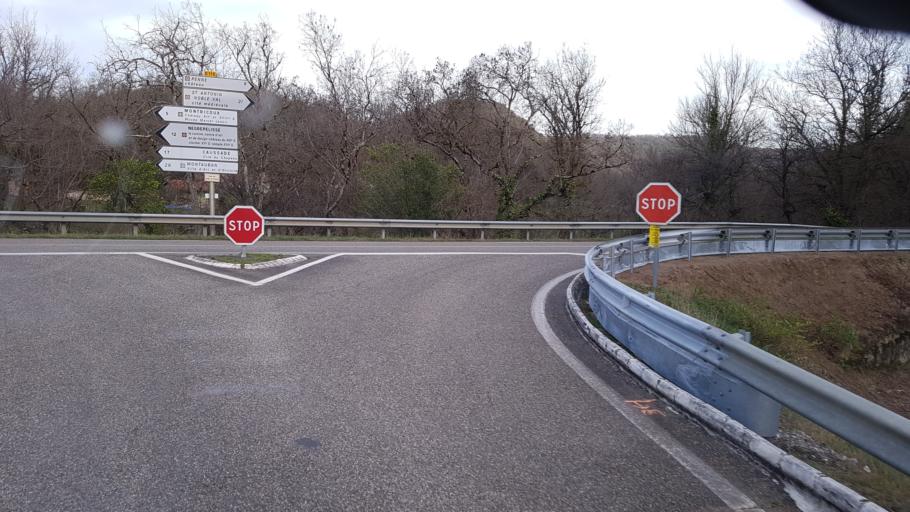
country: FR
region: Midi-Pyrenees
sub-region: Departement du Tarn-et-Garonne
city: Montricoux
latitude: 44.0564
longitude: 1.6709
